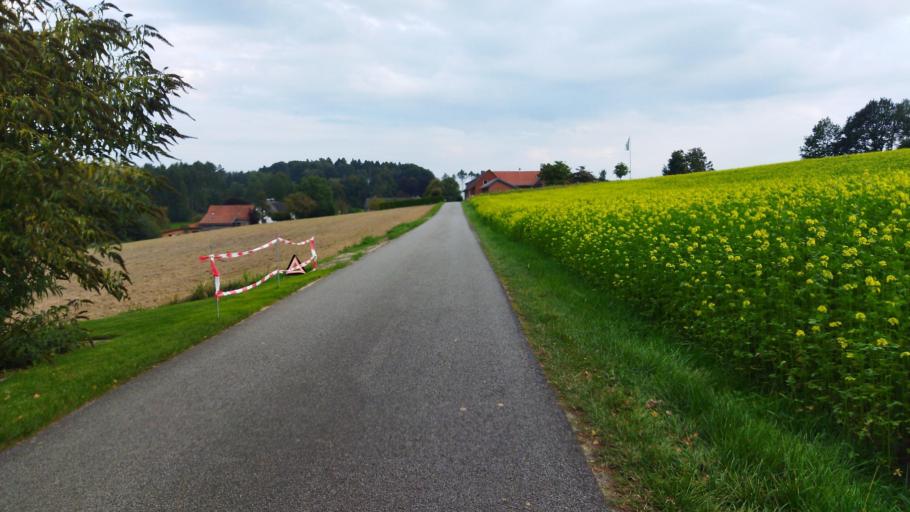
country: DE
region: Lower Saxony
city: Bad Iburg
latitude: 52.1745
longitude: 8.0136
